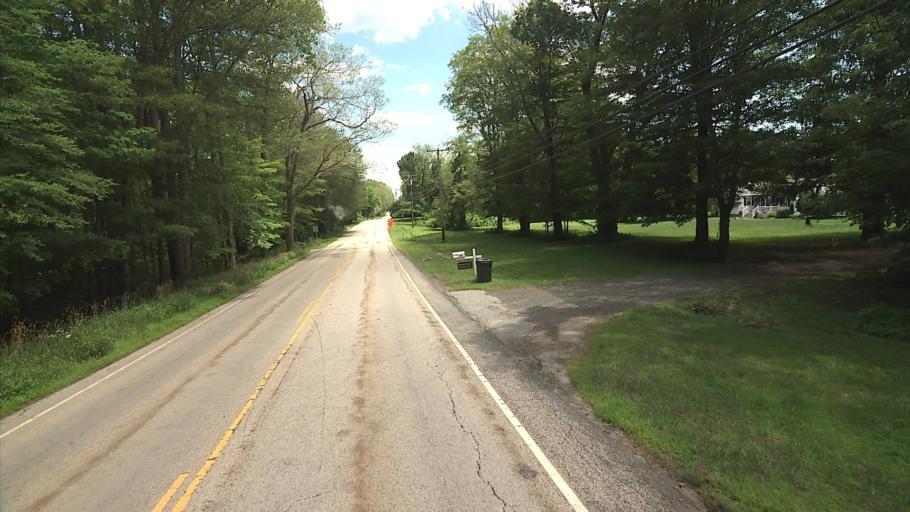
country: US
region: Connecticut
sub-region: Middlesex County
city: Moodus
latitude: 41.4709
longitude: -72.4022
